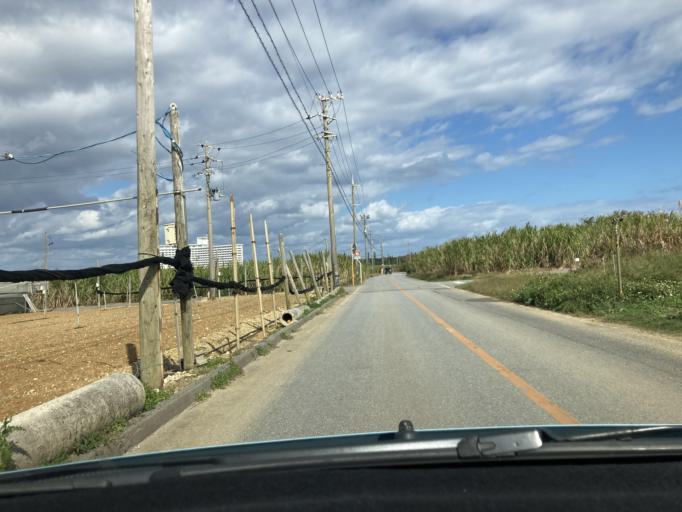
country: JP
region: Okinawa
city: Ishikawa
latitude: 26.4280
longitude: 127.7181
